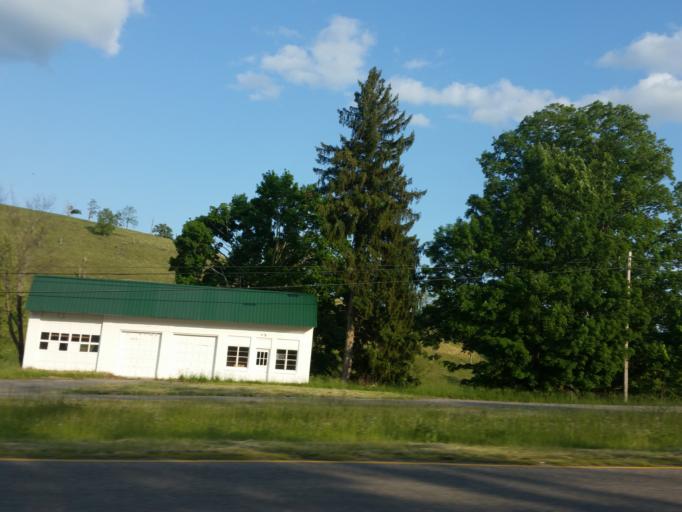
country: US
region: Virginia
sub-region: Russell County
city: Honaker
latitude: 36.9370
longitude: -81.9667
